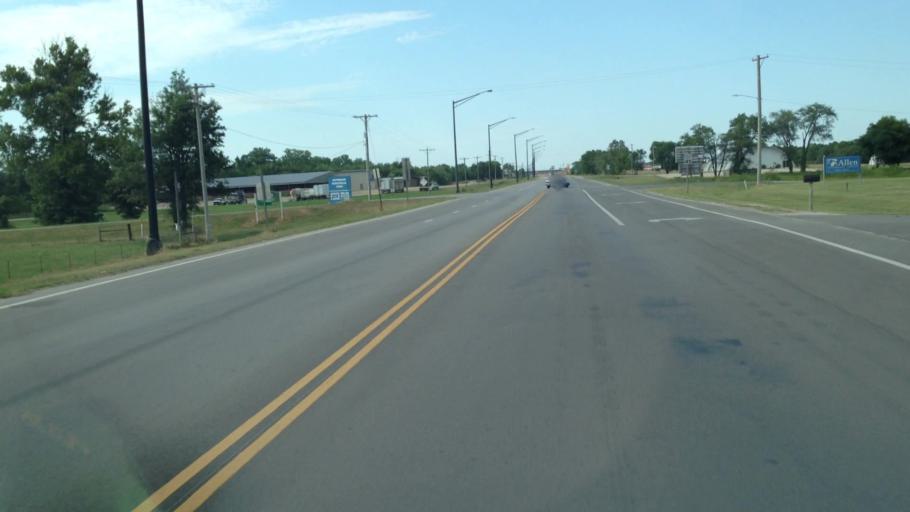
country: US
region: Kansas
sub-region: Labette County
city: Parsons
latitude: 37.3543
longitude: -95.2589
